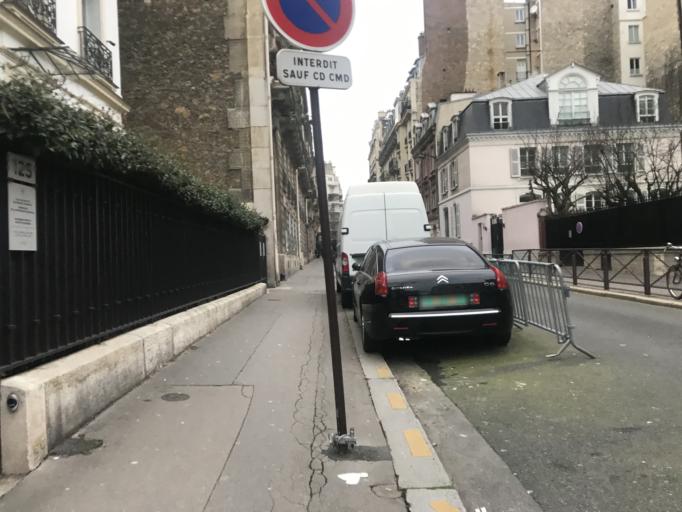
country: FR
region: Ile-de-France
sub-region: Departement des Hauts-de-Seine
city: Neuilly-sur-Seine
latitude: 48.8563
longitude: 2.2682
